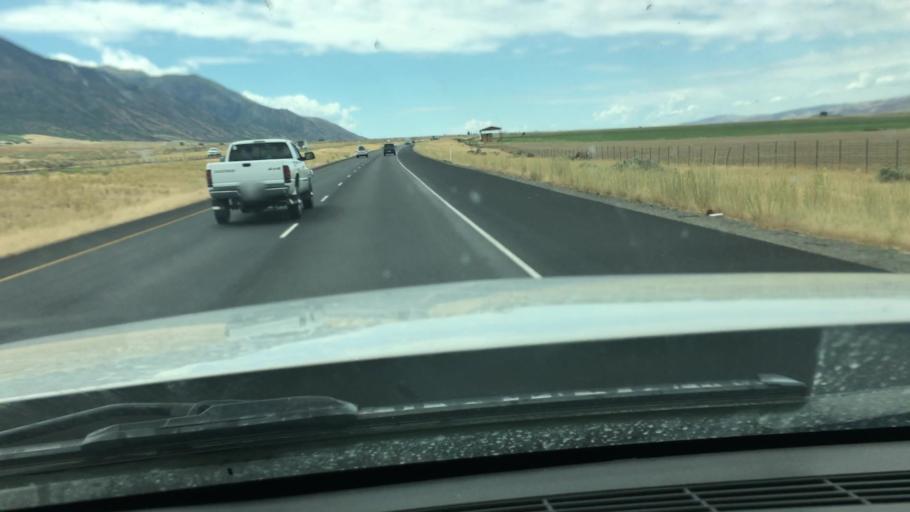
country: US
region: Utah
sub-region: Juab County
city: Mona
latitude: 39.8835
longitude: -111.8285
